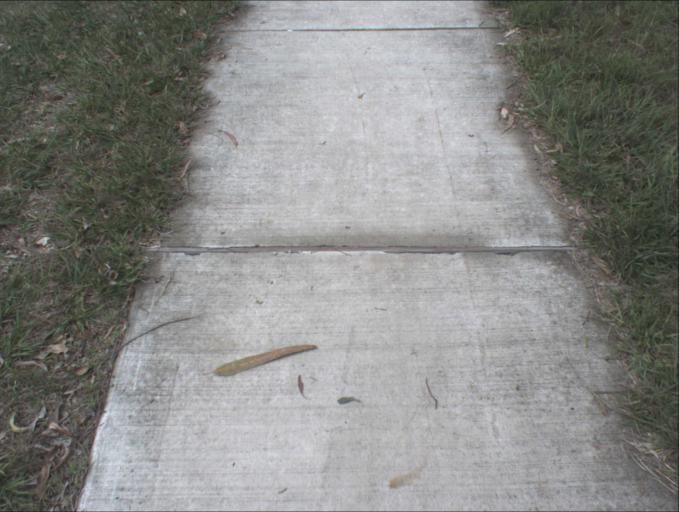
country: AU
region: Queensland
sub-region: Logan
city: Park Ridge South
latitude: -27.7154
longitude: 152.9790
